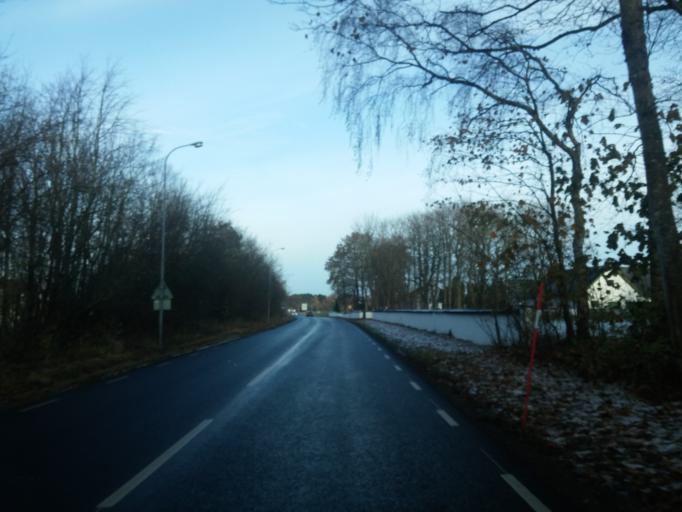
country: SE
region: Skane
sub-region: Angelholms Kommun
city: AEngelholm
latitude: 56.2241
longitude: 12.8338
